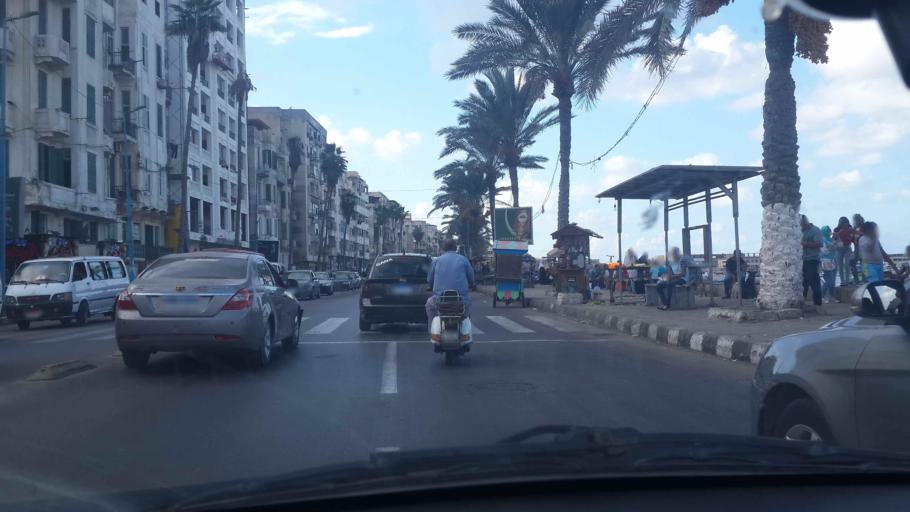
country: EG
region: Alexandria
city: Alexandria
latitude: 31.2062
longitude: 29.8839
